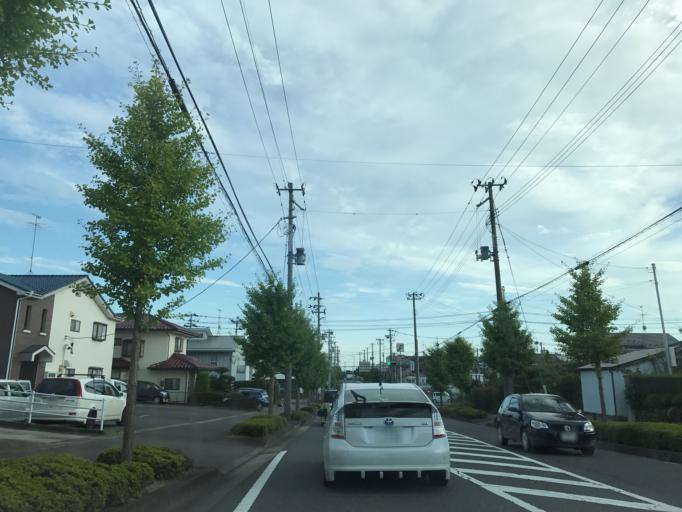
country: JP
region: Fukushima
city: Sukagawa
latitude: 37.3044
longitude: 140.3594
